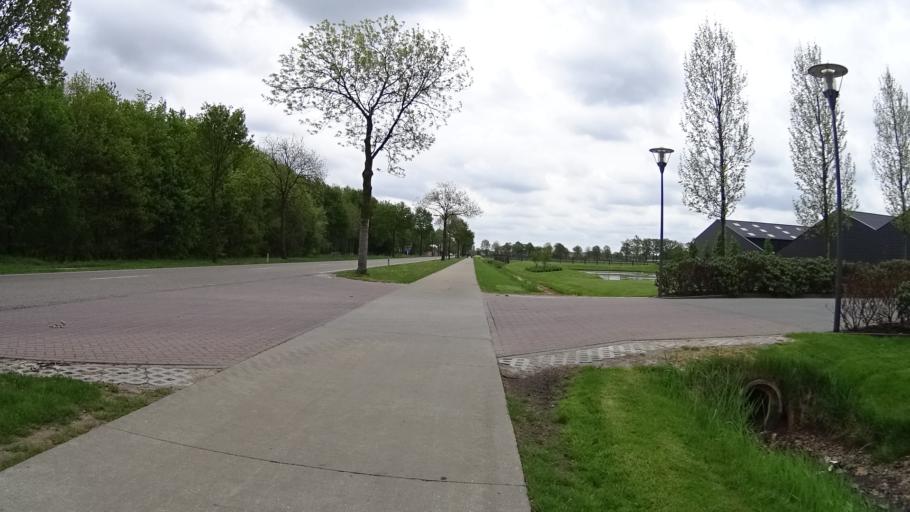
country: NL
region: North Brabant
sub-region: Gemeente Veghel
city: Keldonk
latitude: 51.6062
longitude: 5.5760
